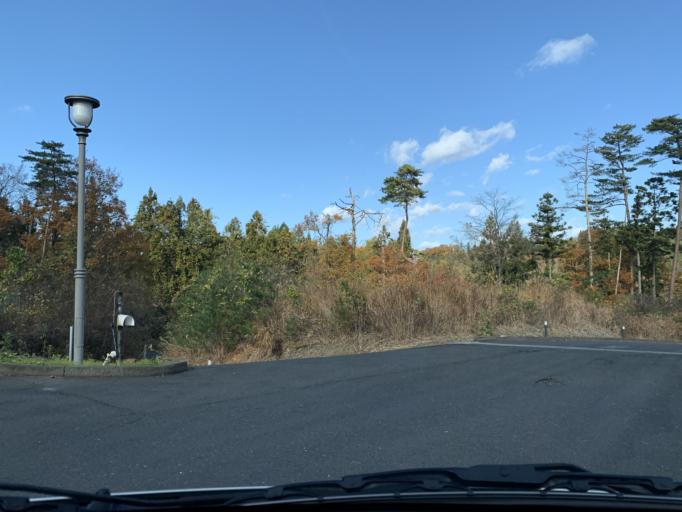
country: JP
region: Iwate
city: Mizusawa
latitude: 39.0420
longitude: 141.1016
